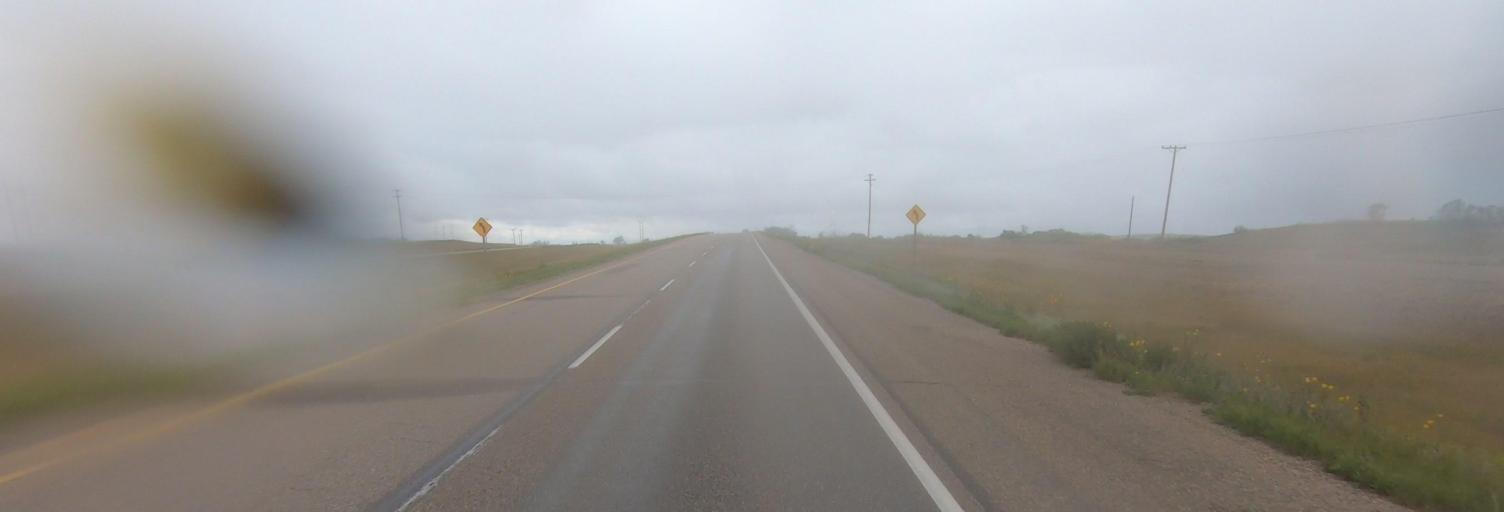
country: CA
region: Saskatchewan
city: Swift Current
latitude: 50.3874
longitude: -107.4689
